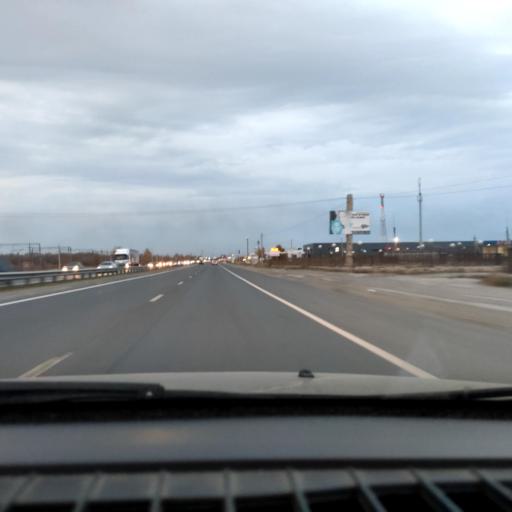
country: RU
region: Samara
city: Tol'yatti
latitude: 53.5727
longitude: 49.3884
